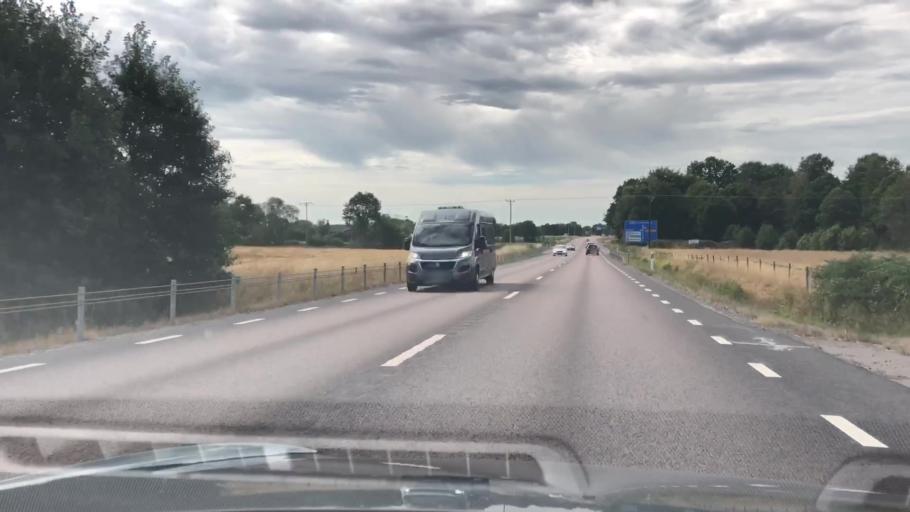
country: SE
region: Kalmar
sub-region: Torsas Kommun
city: Torsas
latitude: 56.3280
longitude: 16.0400
